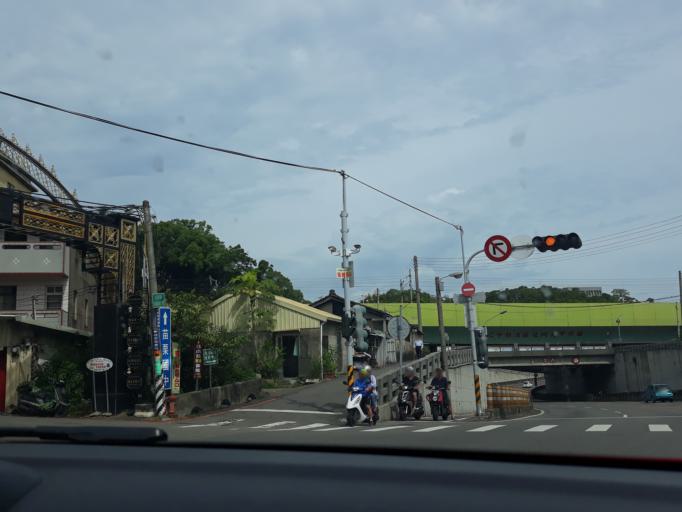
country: TW
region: Taiwan
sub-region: Miaoli
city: Miaoli
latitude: 24.5550
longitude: 120.8141
